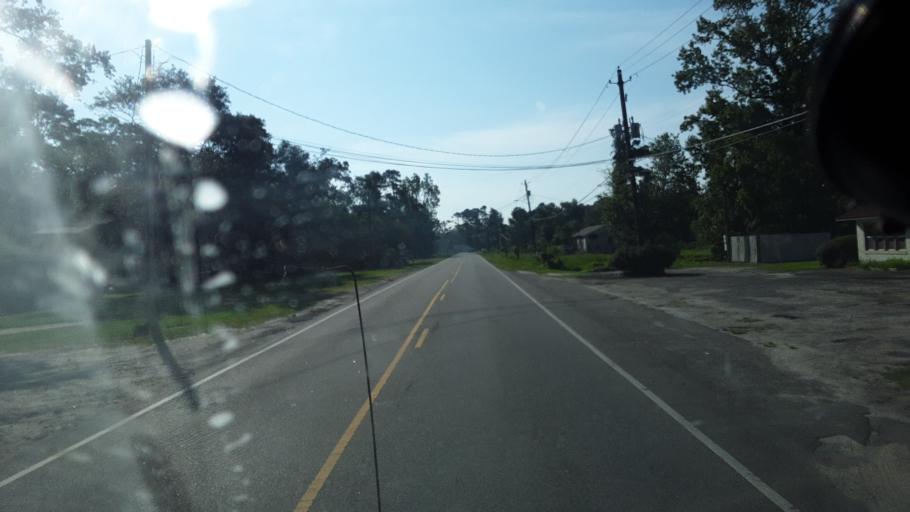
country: US
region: North Carolina
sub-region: Brunswick County
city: Leland
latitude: 34.2546
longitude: -78.0415
